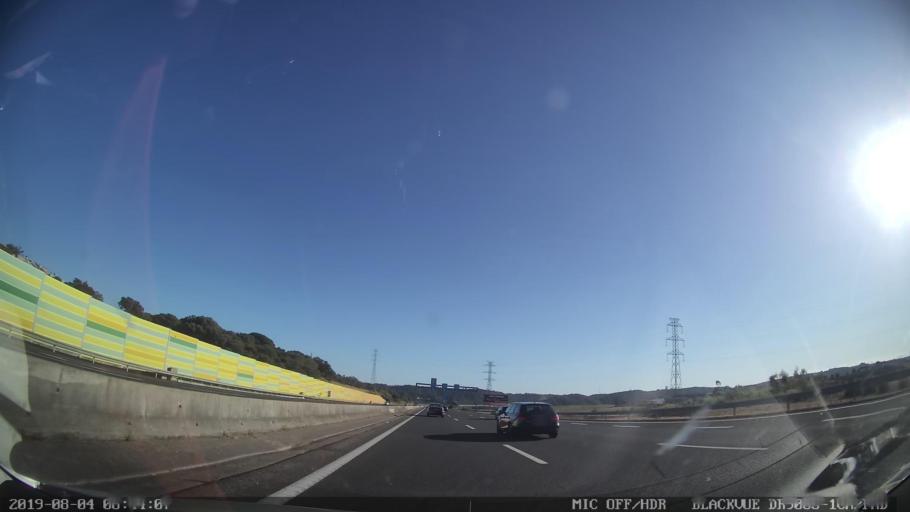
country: PT
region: Santarem
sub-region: Santarem
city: Santarem
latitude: 39.2544
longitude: -8.7363
